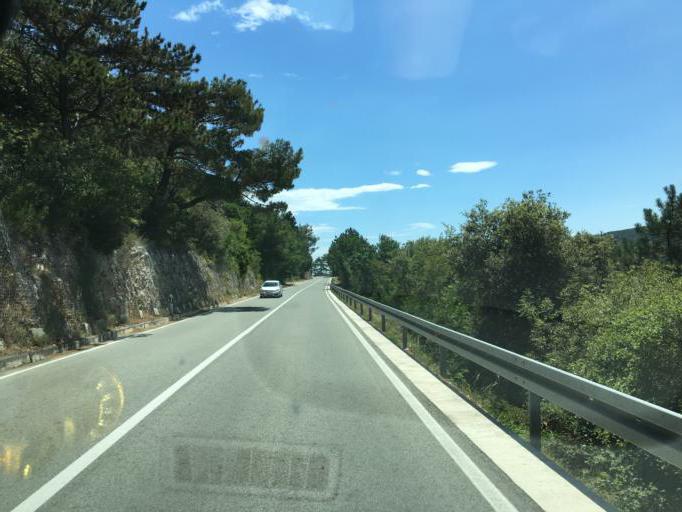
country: HR
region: Istarska
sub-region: Grad Labin
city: Rabac
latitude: 45.1348
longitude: 14.1859
